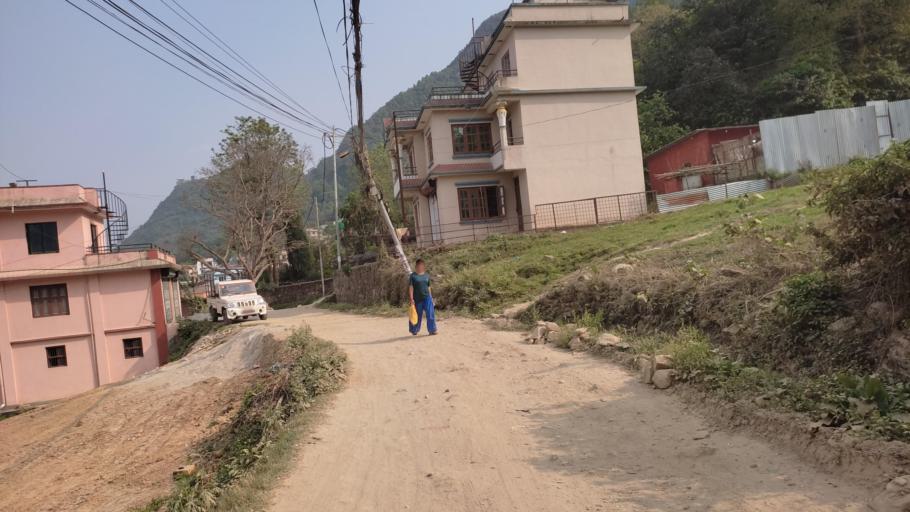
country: NP
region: Central Region
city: Kirtipur
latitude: 27.6624
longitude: 85.2583
